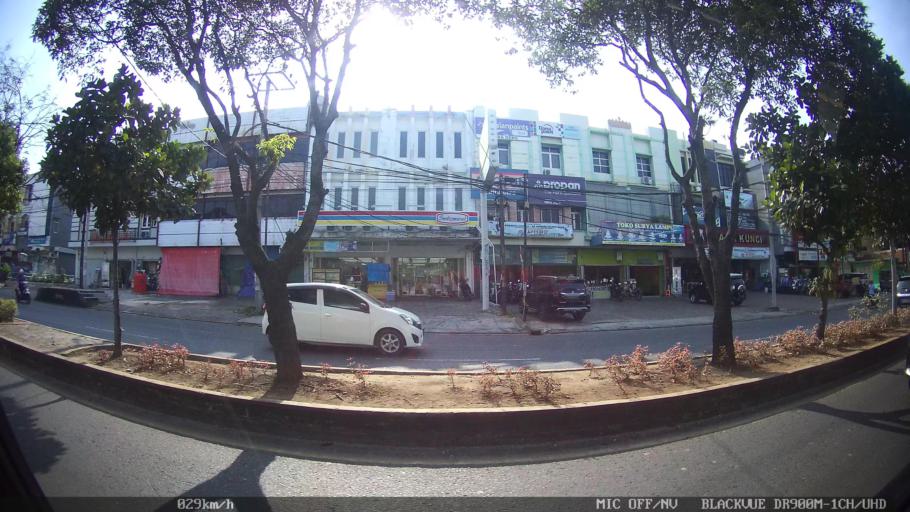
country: ID
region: Lampung
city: Kedaton
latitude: -5.3973
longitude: 105.2618
